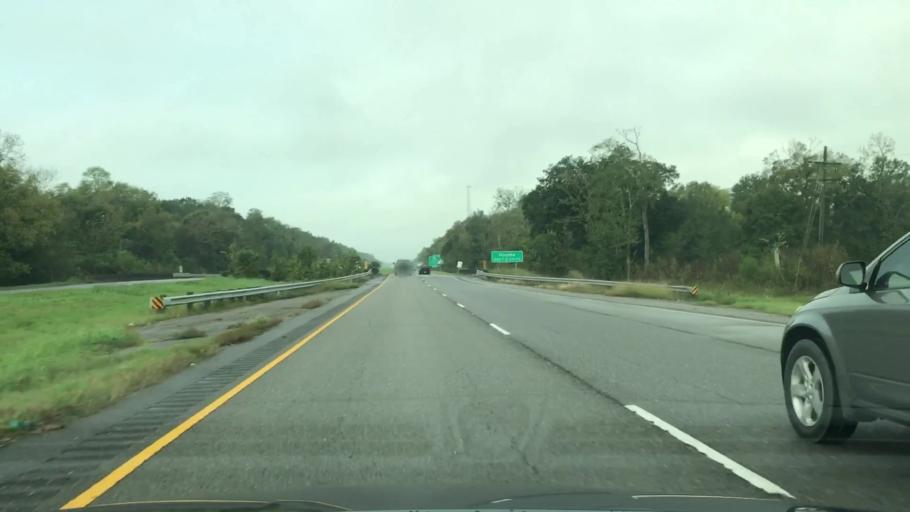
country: US
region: Louisiana
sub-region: Terrebonne Parish
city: Gray
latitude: 29.6820
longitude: -90.7590
